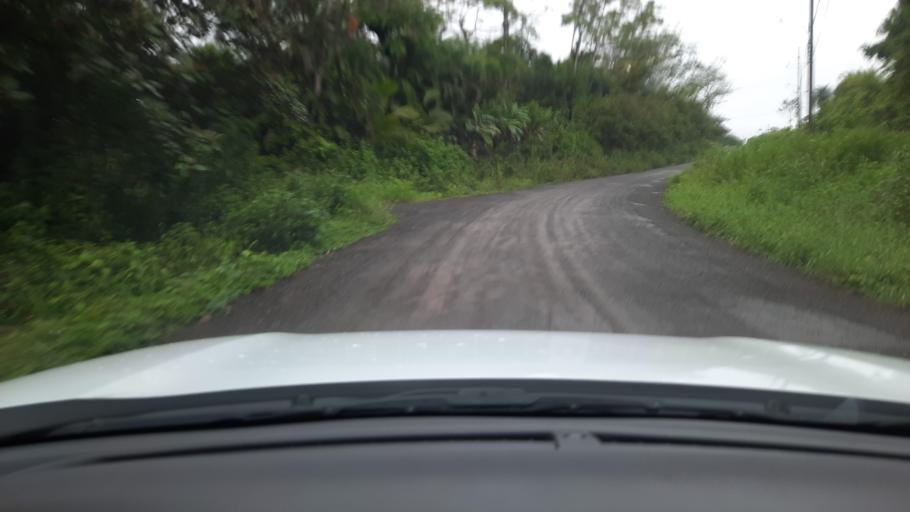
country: CR
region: Alajuela
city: San Jose
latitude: 11.0135
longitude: -85.3270
